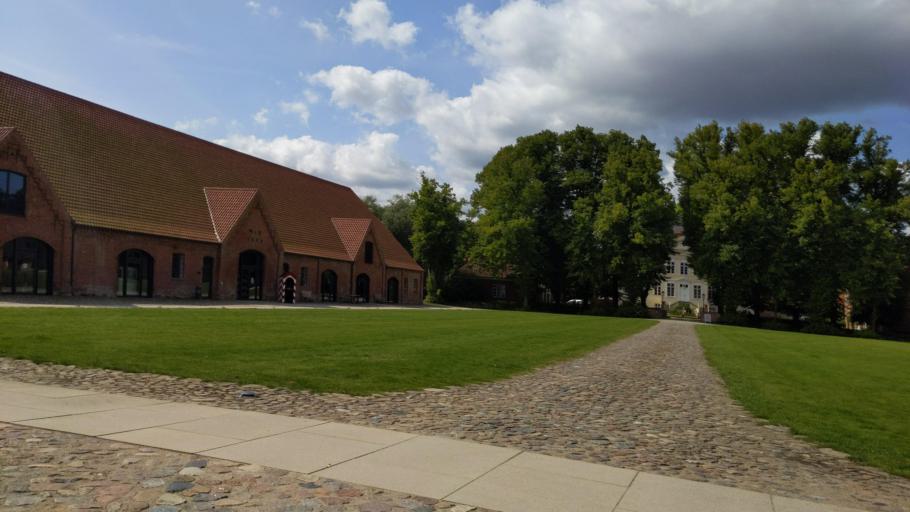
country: DE
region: Schleswig-Holstein
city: Altenkrempe
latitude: 54.1402
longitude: 10.8169
